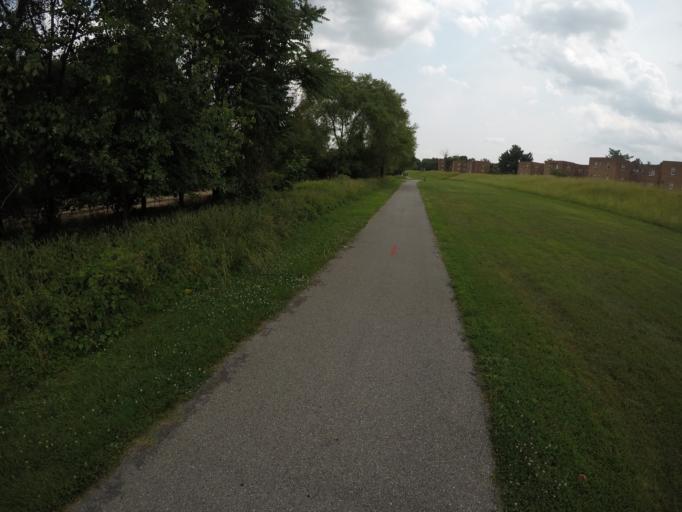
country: US
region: Maryland
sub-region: Prince George's County
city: Brentwood
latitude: 38.9514
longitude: -76.9615
